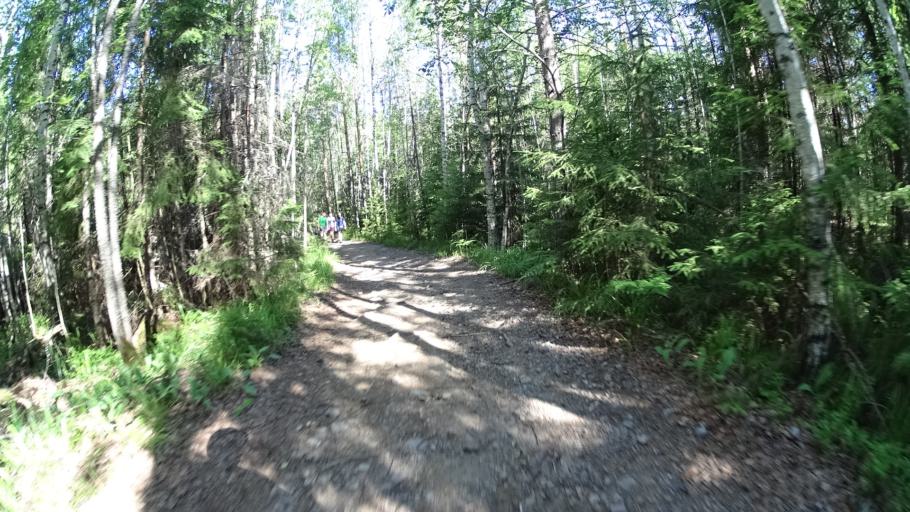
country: FI
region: Uusimaa
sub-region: Helsinki
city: Espoo
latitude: 60.3177
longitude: 24.5013
